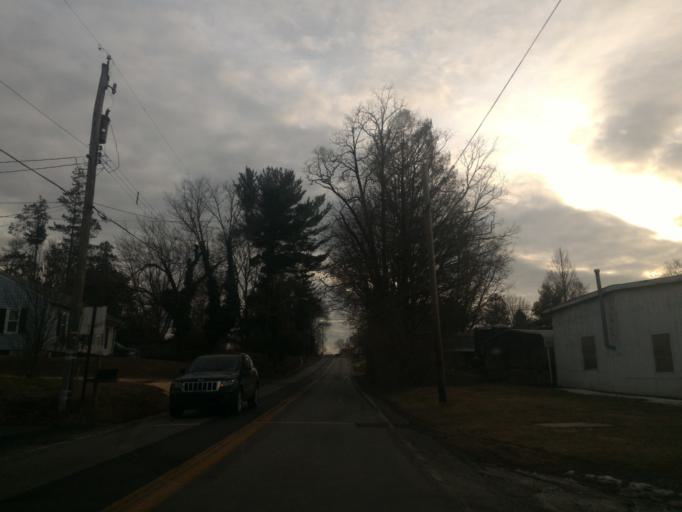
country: US
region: Pennsylvania
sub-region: York County
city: Jacobus
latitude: 39.8823
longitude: -76.7086
